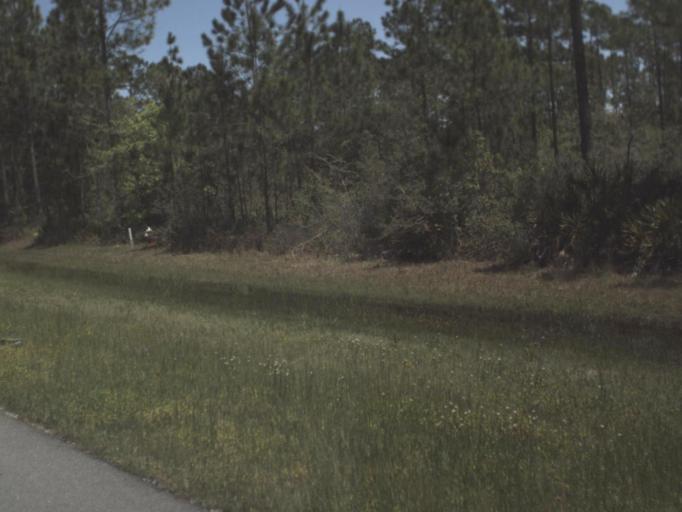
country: US
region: Florida
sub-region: Escambia County
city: Myrtle Grove
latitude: 30.4081
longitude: -87.3420
